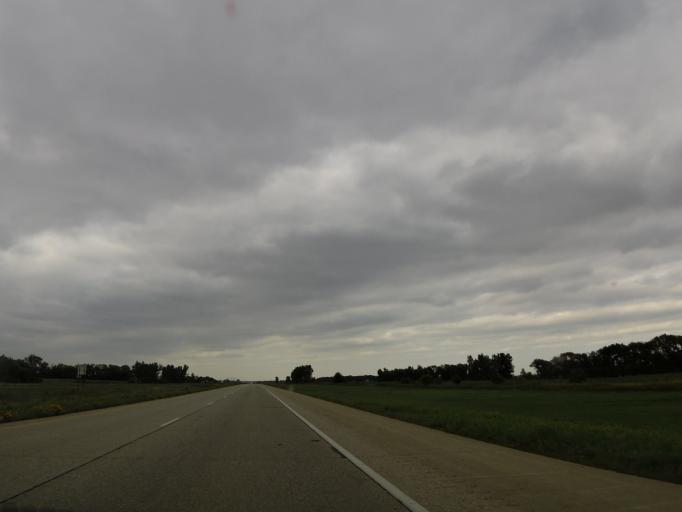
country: US
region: North Dakota
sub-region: Richland County
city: Wahpeton
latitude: 46.1040
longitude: -96.8352
